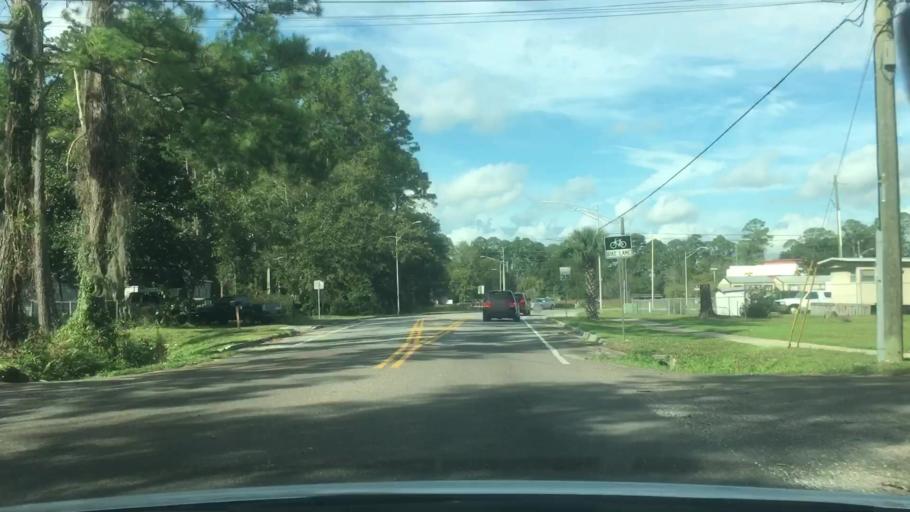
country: US
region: Florida
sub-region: Nassau County
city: Yulee
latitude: 30.4883
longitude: -81.6231
